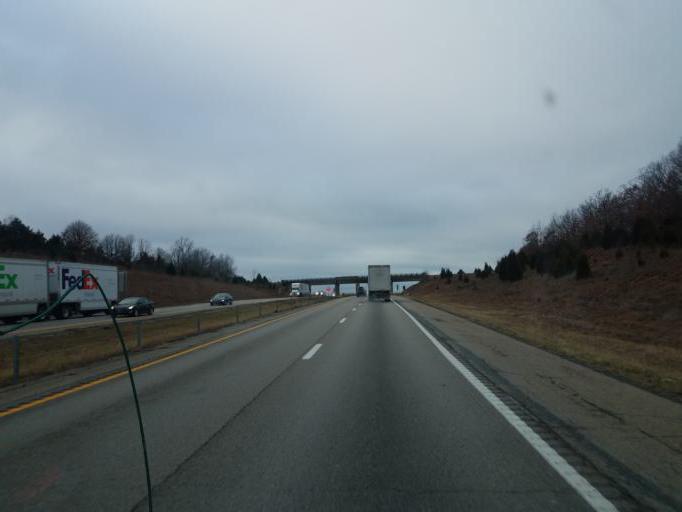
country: US
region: Missouri
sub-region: Laclede County
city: Lebanon
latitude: 37.5637
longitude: -92.7812
